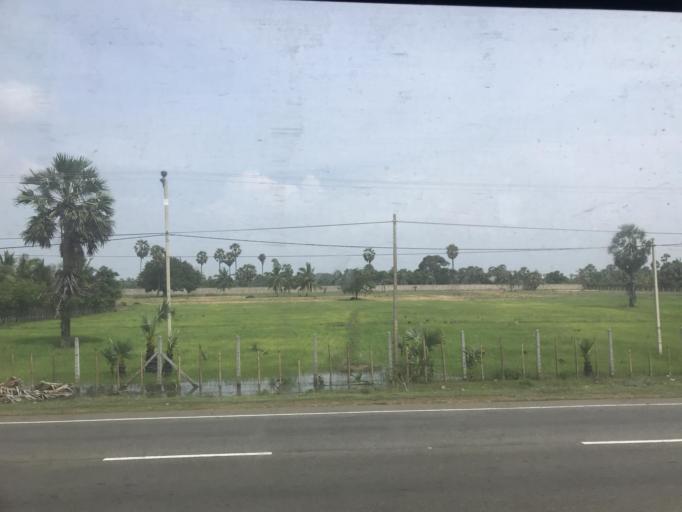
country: LK
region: Northern Province
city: Point Pedro
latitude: 9.6224
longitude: 80.3130
